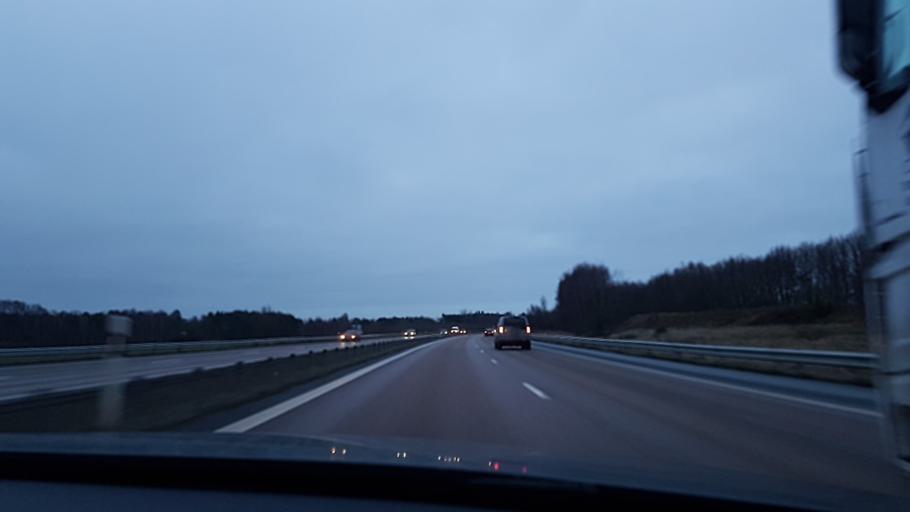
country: SE
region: Skane
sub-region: Kavlinge Kommun
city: Hofterup
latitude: 55.8001
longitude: 12.9610
